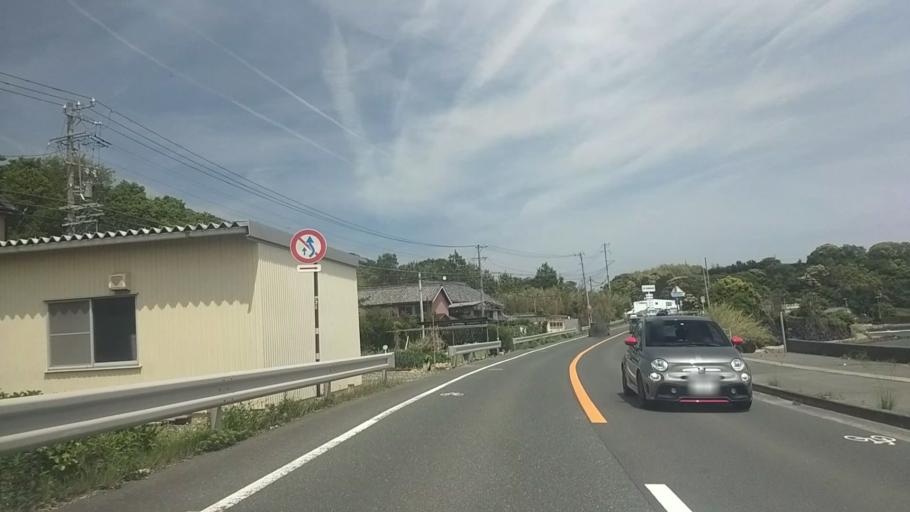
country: JP
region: Shizuoka
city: Kosai-shi
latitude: 34.7634
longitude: 137.5231
